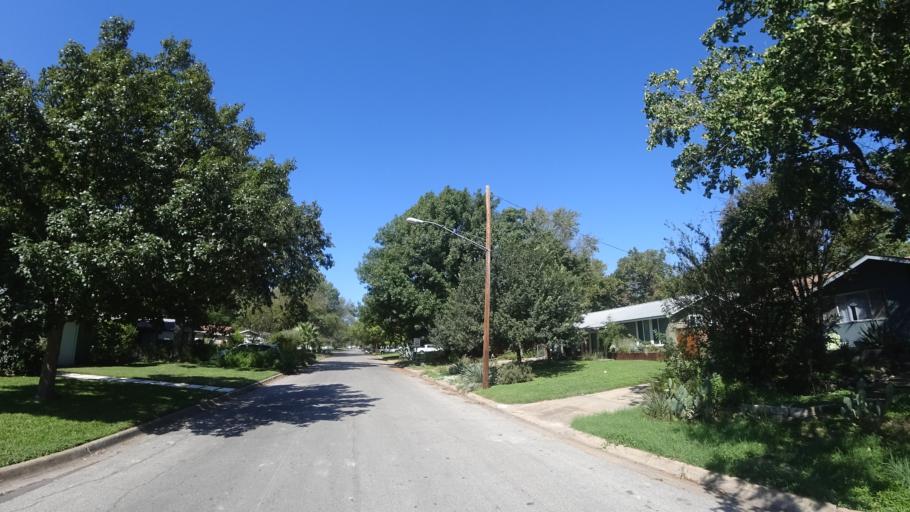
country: US
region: Texas
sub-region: Travis County
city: Austin
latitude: 30.3067
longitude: -97.6981
